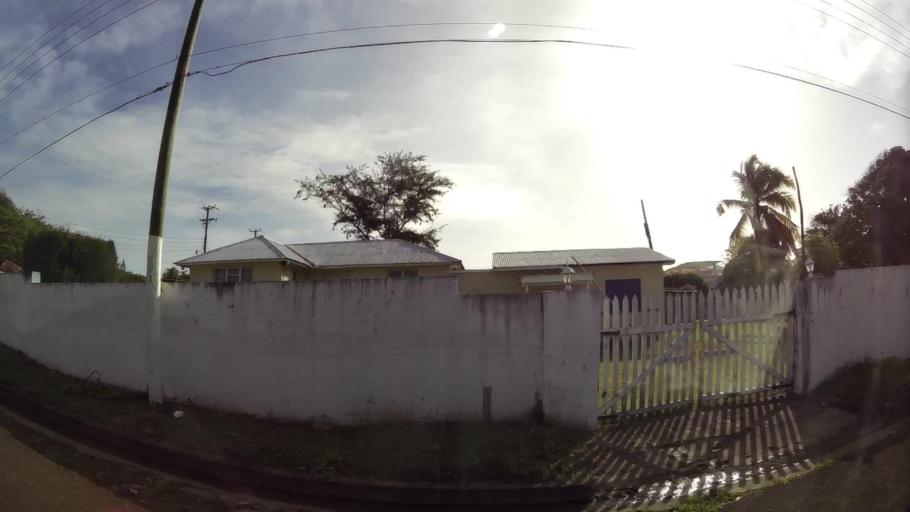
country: KN
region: Saint George Basseterre
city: Basseterre
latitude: 17.2924
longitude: -62.7347
